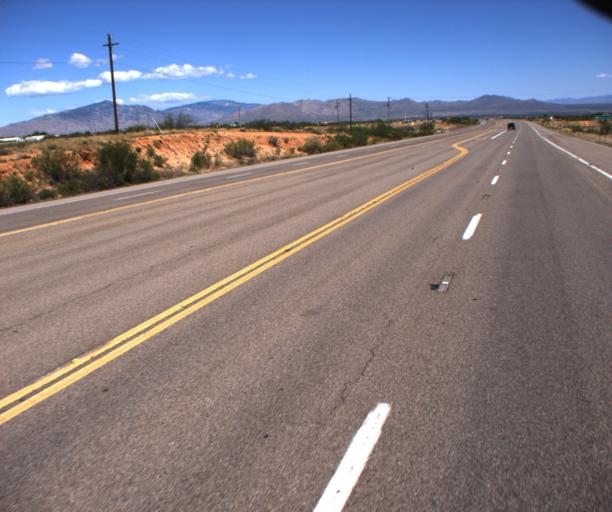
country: US
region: Arizona
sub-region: Cochise County
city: Whetstone
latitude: 31.9466
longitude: -110.3411
